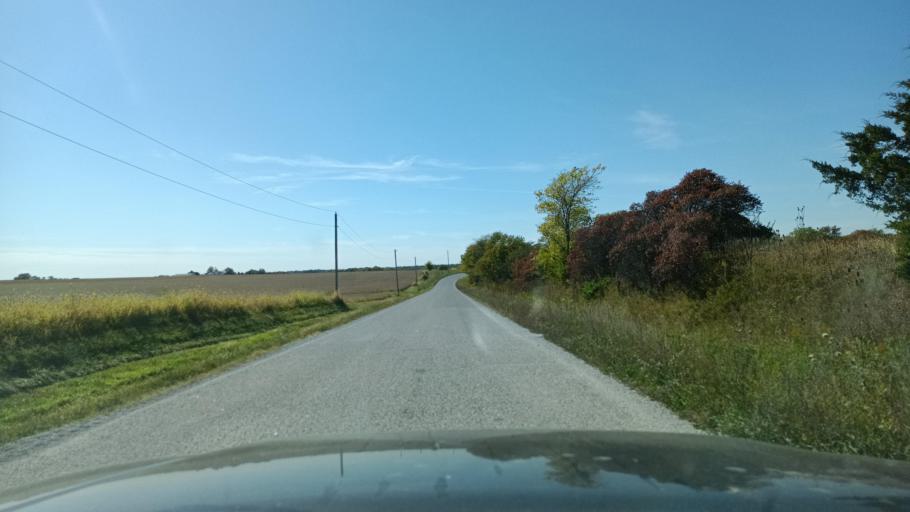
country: US
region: Illinois
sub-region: Logan County
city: Atlanta
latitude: 40.2341
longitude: -89.1526
